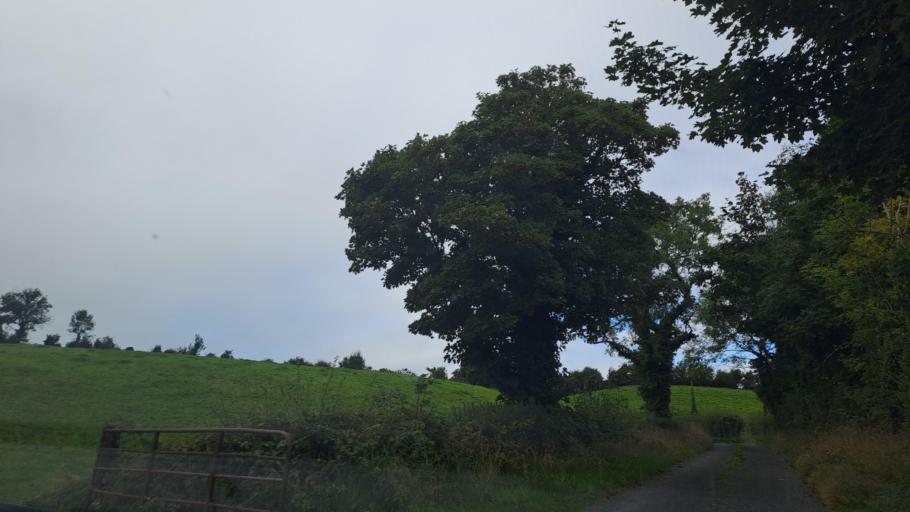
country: IE
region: Ulster
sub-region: County Monaghan
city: Carrickmacross
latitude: 53.9866
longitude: -6.7934
